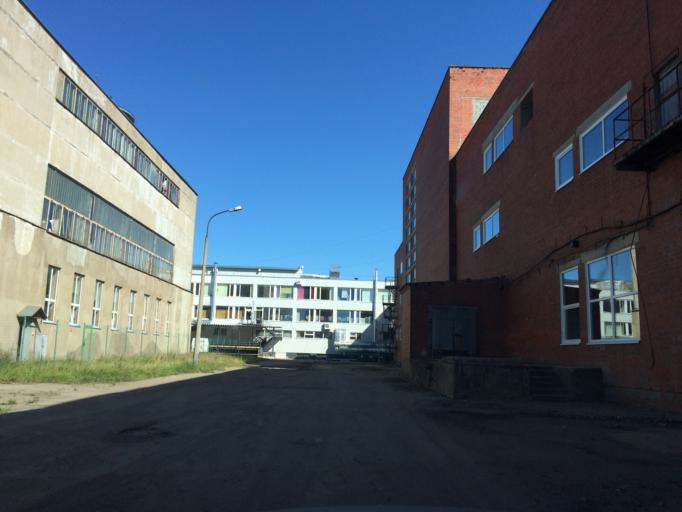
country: LV
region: Rezekne
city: Rezekne
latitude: 56.5280
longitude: 27.3417
